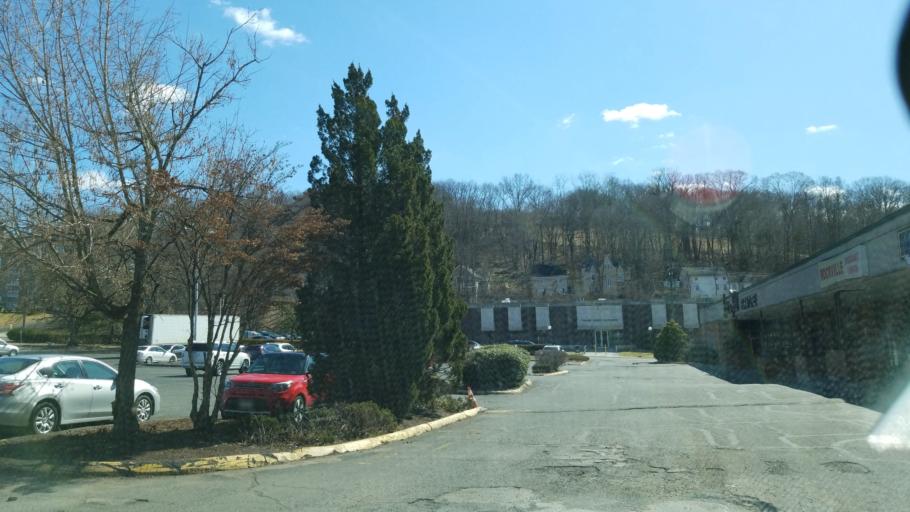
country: US
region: Connecticut
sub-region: Tolland County
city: Rockville
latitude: 41.8670
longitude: -72.4476
